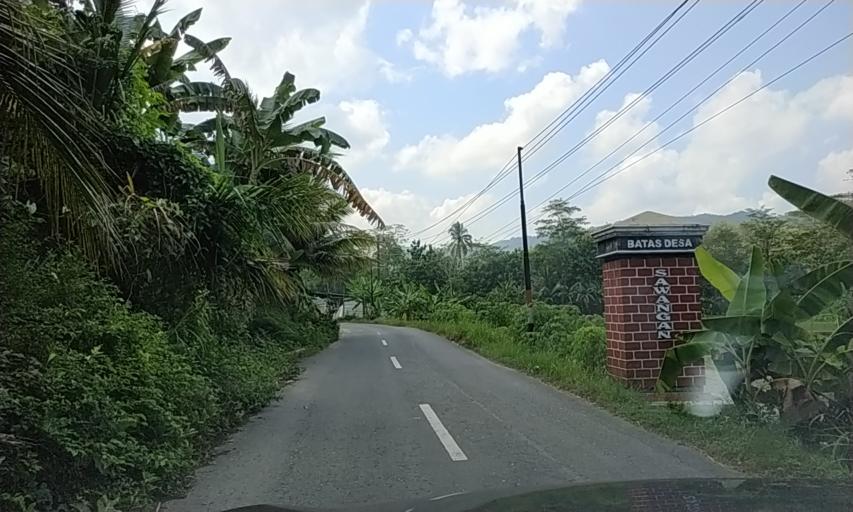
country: ID
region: Central Java
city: Gombong
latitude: -7.6325
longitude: 109.7148
